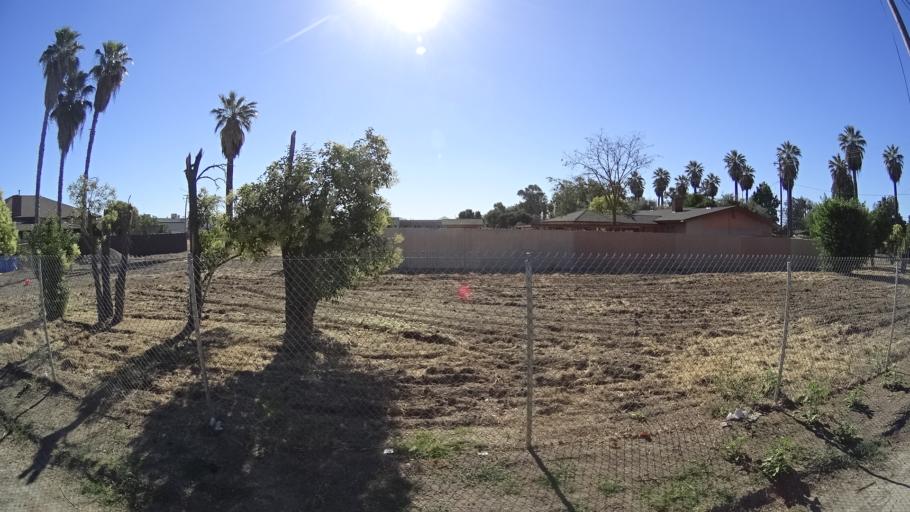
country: US
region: California
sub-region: Fresno County
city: West Park
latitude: 36.7291
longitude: -119.8265
